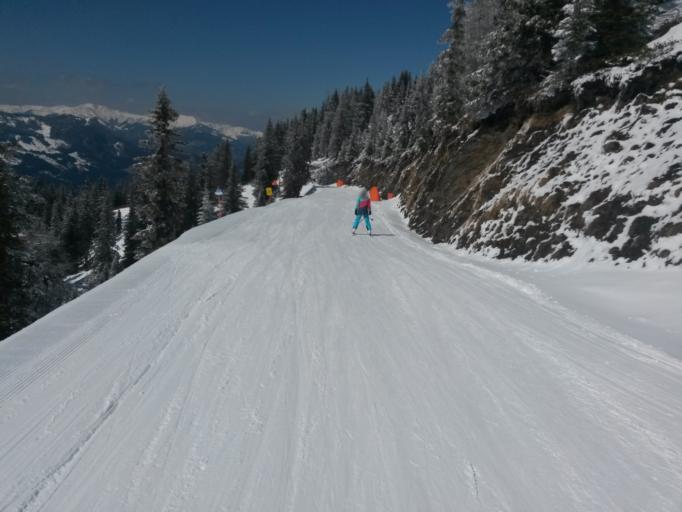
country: AT
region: Salzburg
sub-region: Politischer Bezirk Sankt Johann im Pongau
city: Dorfgastein
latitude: 47.2332
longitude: 13.1459
